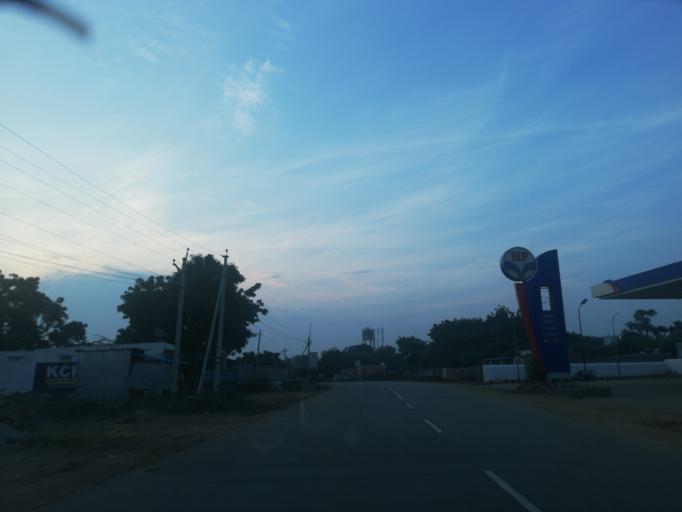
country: IN
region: Andhra Pradesh
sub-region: Guntur
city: Macherla
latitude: 16.5874
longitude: 79.3215
